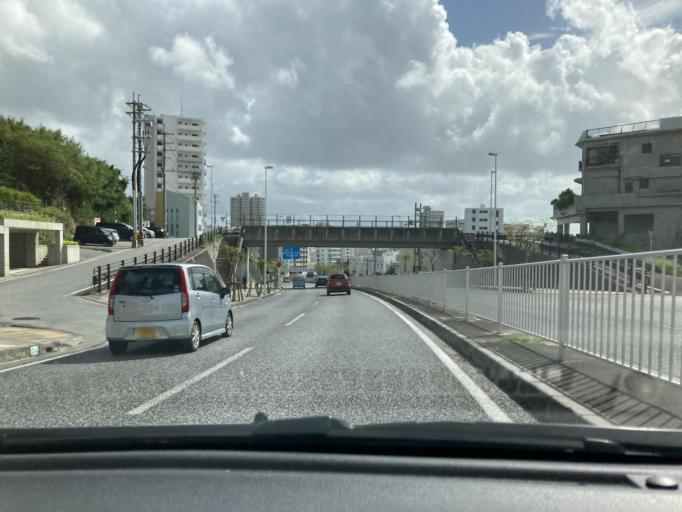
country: JP
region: Okinawa
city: Naha-shi
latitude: 26.2235
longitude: 127.6925
